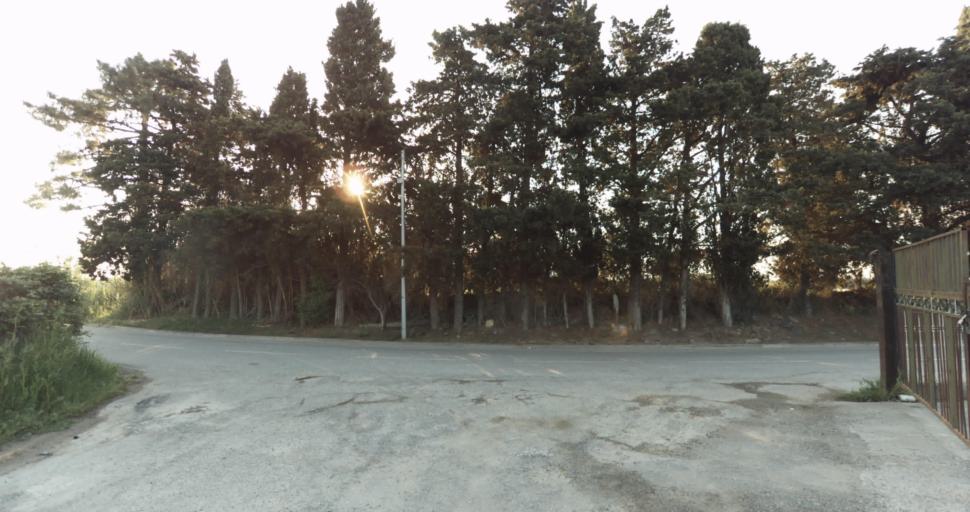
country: FR
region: Corsica
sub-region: Departement de la Haute-Corse
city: Biguglia
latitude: 42.6215
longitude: 9.4434
